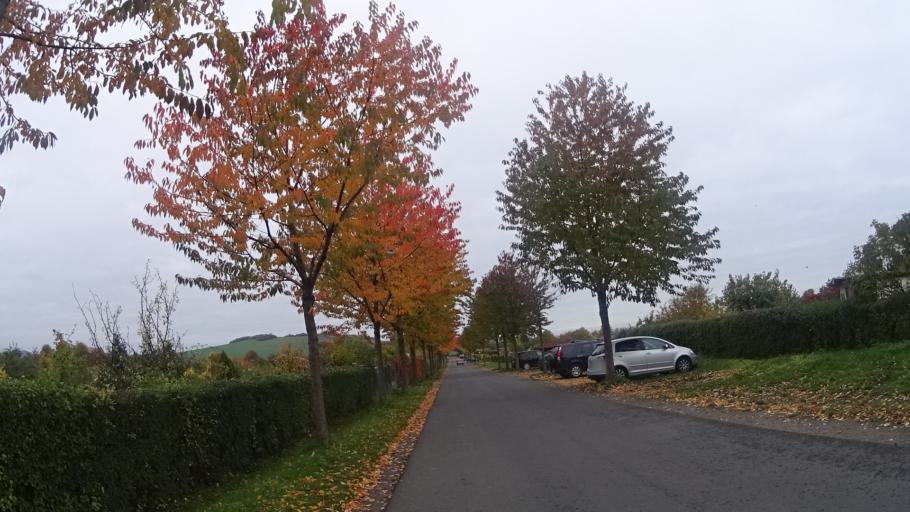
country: DE
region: Thuringia
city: Arnstadt
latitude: 50.8419
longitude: 10.9349
